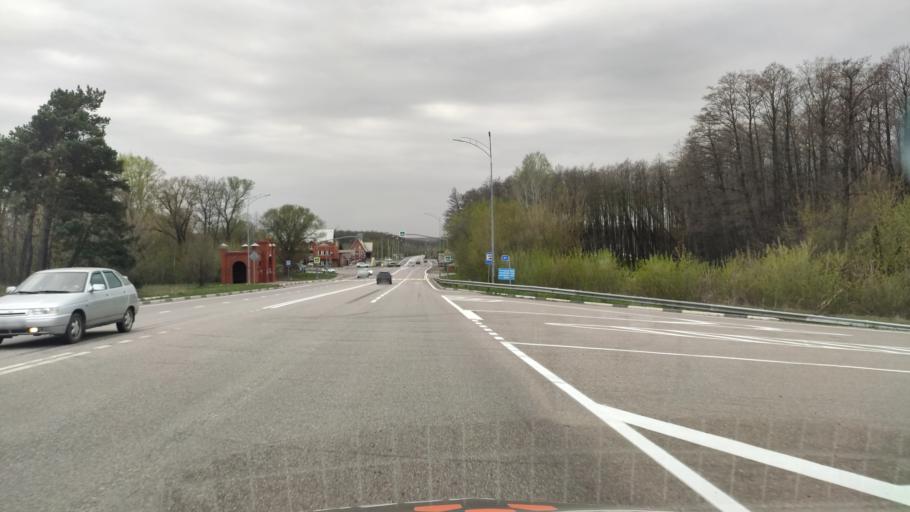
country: RU
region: Belgorod
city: Staryy Oskol
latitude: 51.3576
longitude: 37.8342
